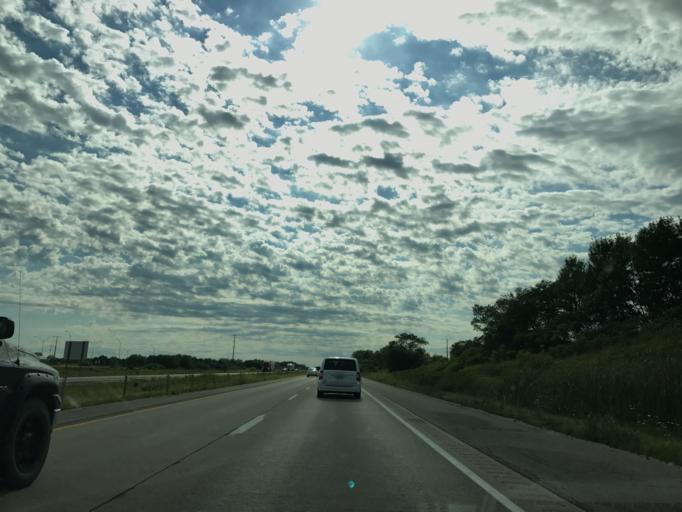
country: US
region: Iowa
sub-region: Dallas County
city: Van Meter
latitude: 41.5568
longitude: -93.9121
